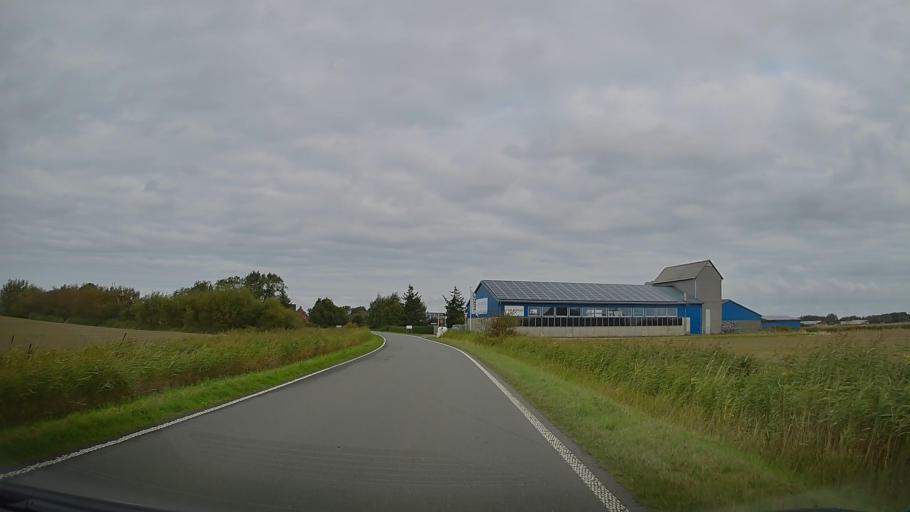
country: DE
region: Schleswig-Holstein
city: Klanxbull
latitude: 54.8821
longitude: 8.6826
